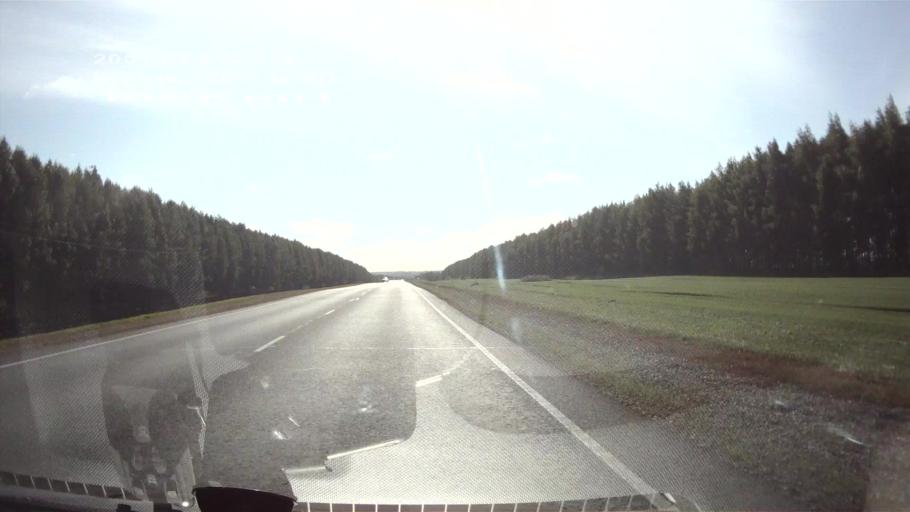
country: RU
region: Ulyanovsk
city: Tsil'na
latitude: 54.5438
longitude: 47.9540
